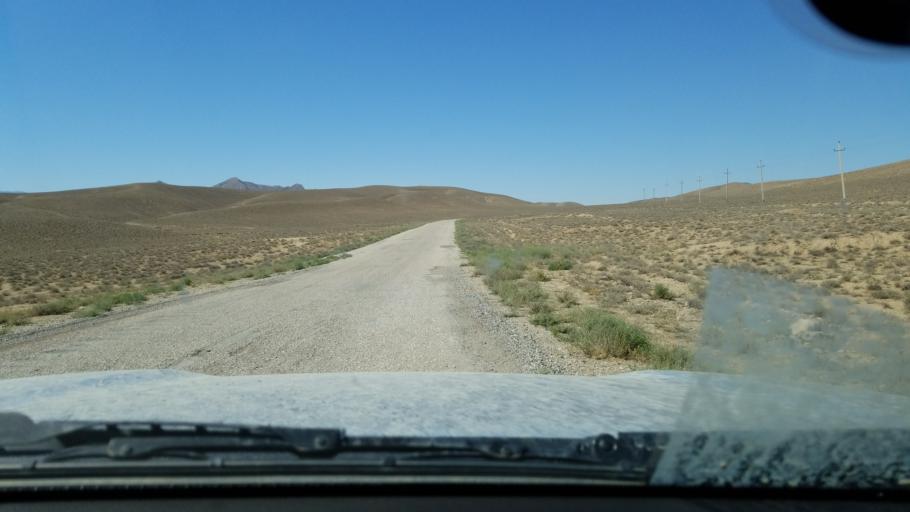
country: TM
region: Balkan
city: Balkanabat
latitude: 39.9062
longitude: 54.4298
